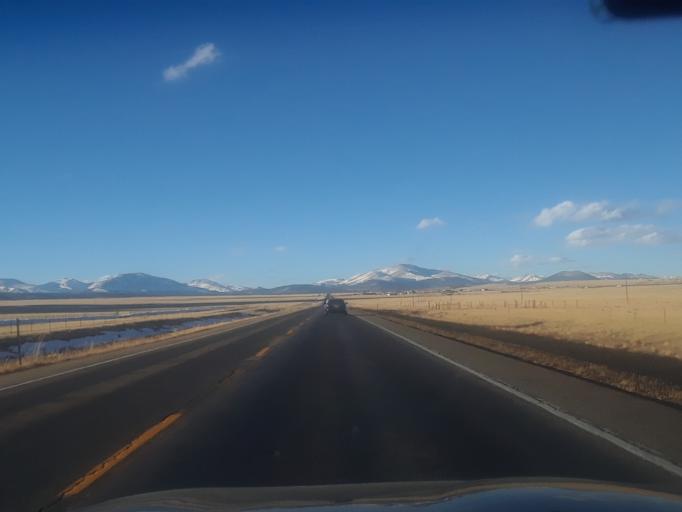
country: US
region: Colorado
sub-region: Park County
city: Fairplay
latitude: 39.0992
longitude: -105.9891
